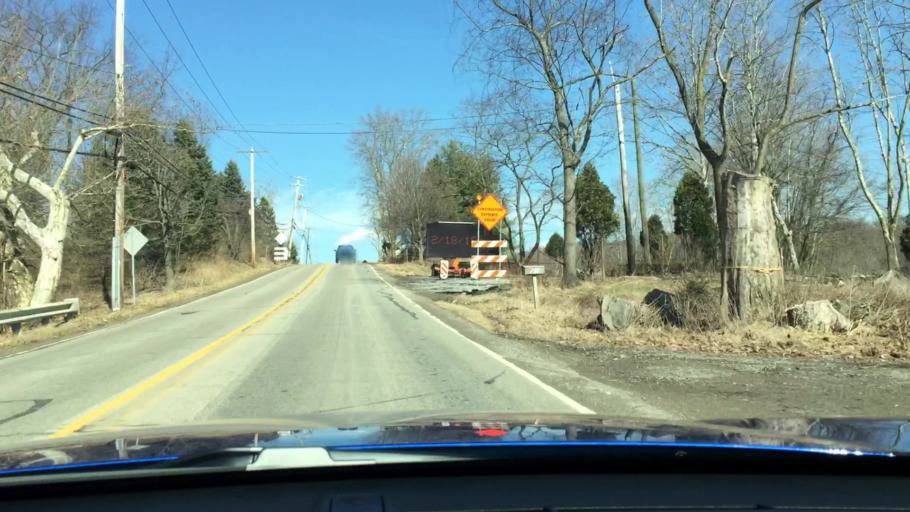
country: US
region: Pennsylvania
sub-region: Washington County
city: Cecil-Bishop
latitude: 40.3042
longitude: -80.1523
